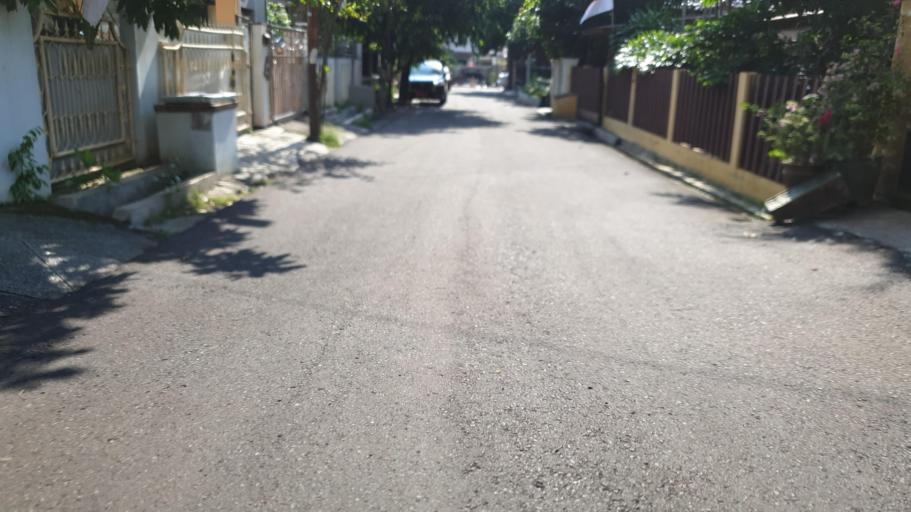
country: ID
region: Jakarta Raya
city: Jakarta
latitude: -6.2886
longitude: 106.8388
